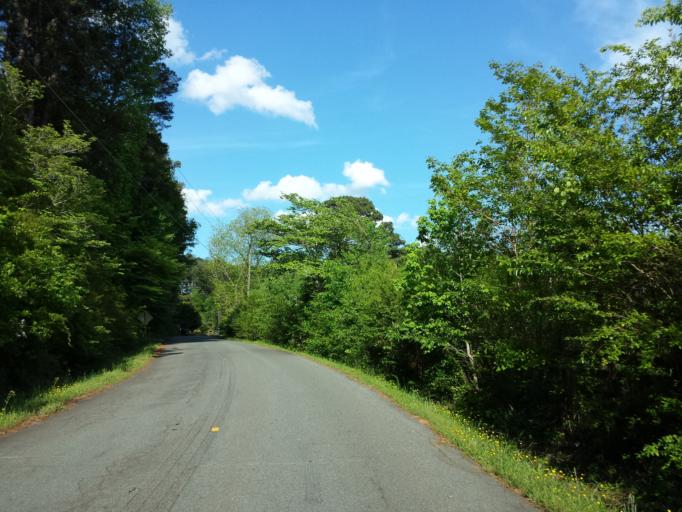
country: US
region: Georgia
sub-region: Cobb County
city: Marietta
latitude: 33.9446
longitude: -84.6169
